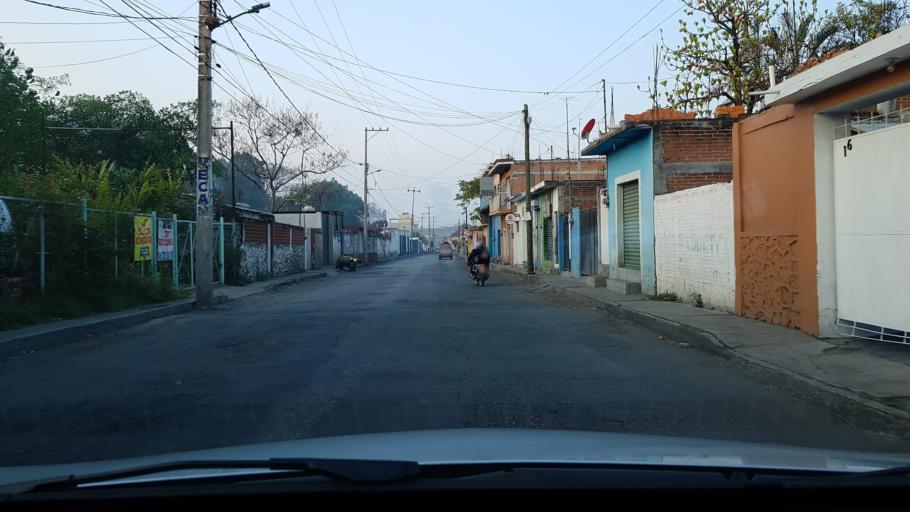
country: MX
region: Morelos
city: Jonacatepec de Leandro Valle
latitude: 18.6851
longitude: -98.8029
